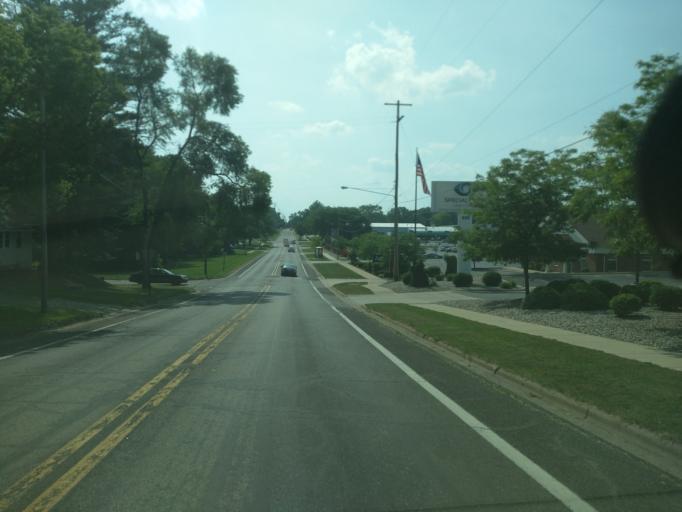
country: US
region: Michigan
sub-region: Jackson County
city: Jackson
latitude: 42.2589
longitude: -84.4250
